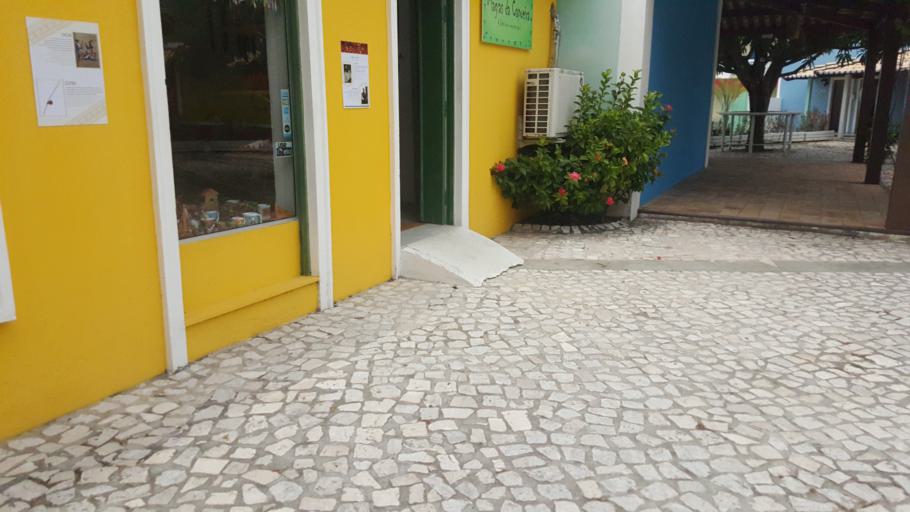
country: BR
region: Bahia
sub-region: Mata De Sao Joao
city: Mata de Sao Joao
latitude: -12.4403
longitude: -37.9229
